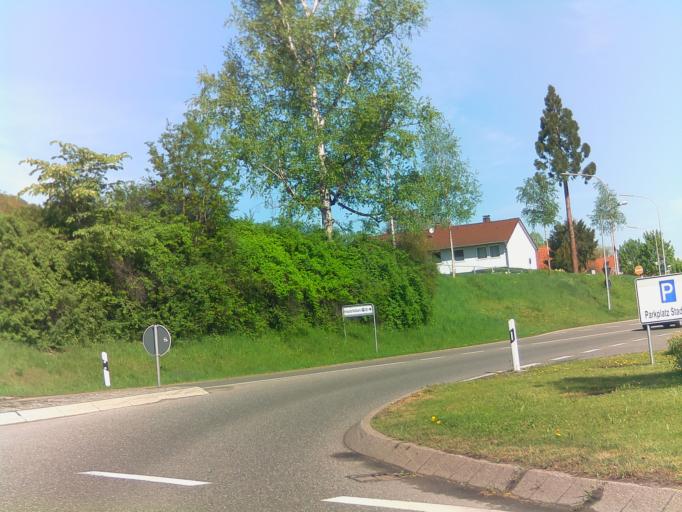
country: DE
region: Baden-Wuerttemberg
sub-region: Karlsruhe Region
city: Nagold
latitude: 48.5497
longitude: 8.7141
